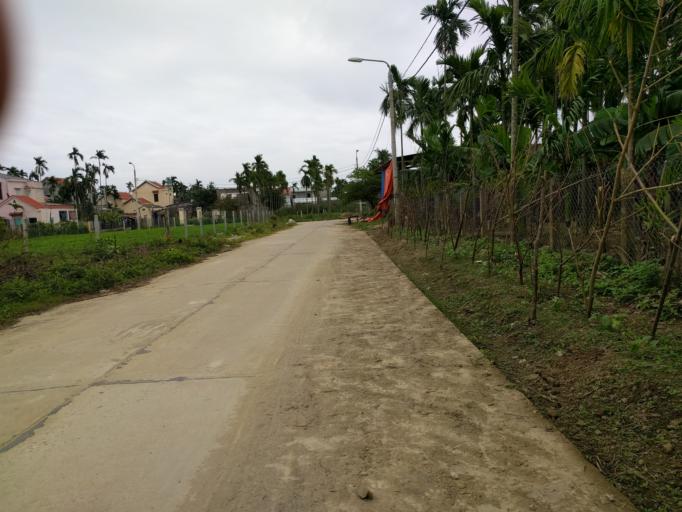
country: VN
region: Quang Nam
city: Hoi An
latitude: 15.8678
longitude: 108.3505
